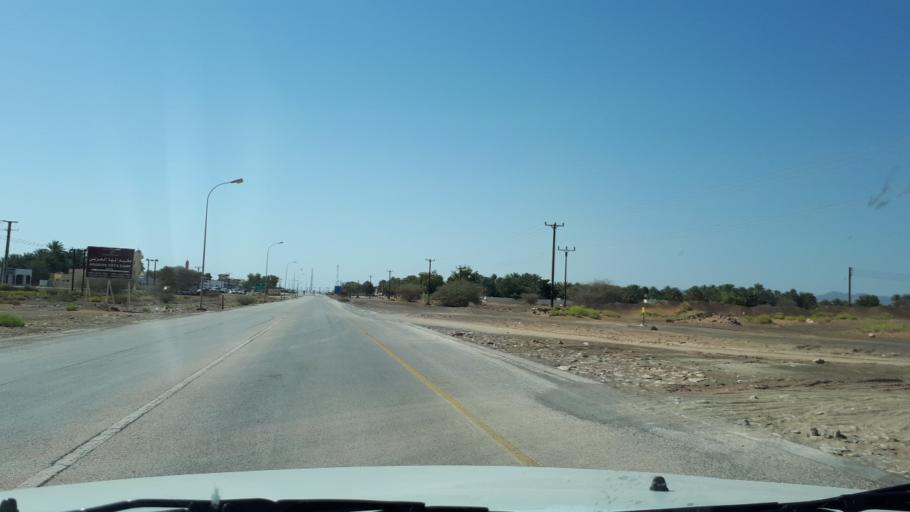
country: OM
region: Ash Sharqiyah
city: Badiyah
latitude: 22.4987
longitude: 58.7520
